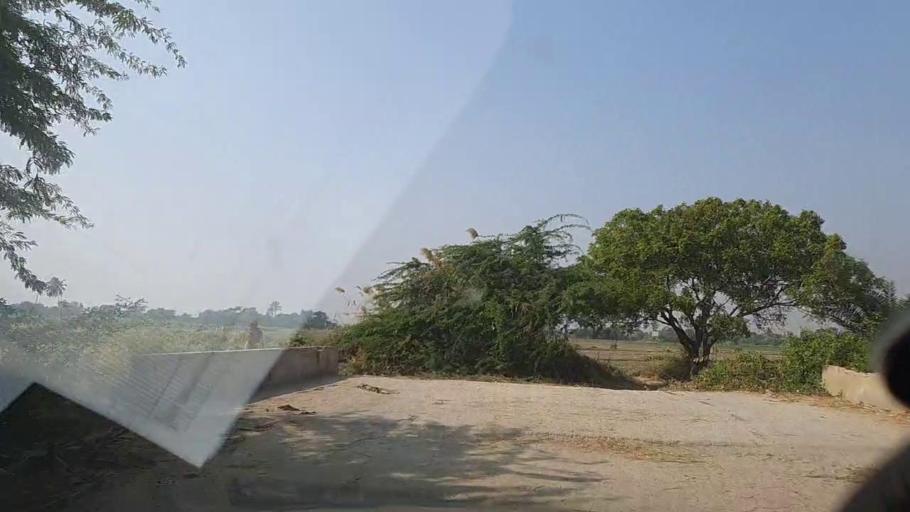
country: PK
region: Sindh
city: Thatta
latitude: 24.6538
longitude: 67.9107
